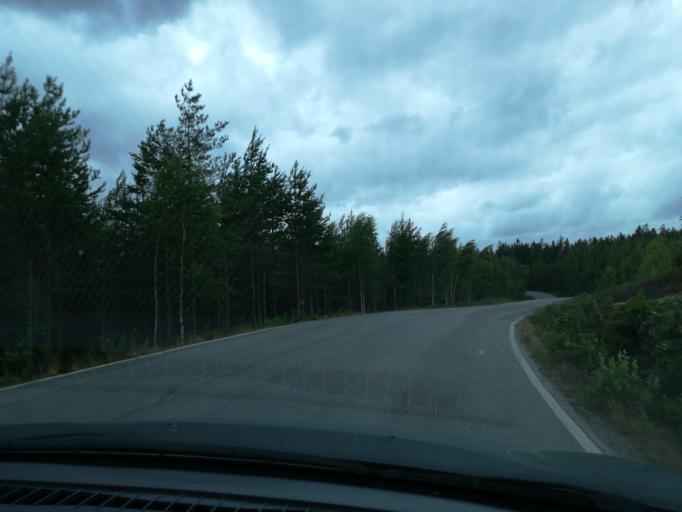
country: FI
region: South Karelia
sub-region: Lappeenranta
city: Savitaipale
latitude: 61.3221
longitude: 27.4851
